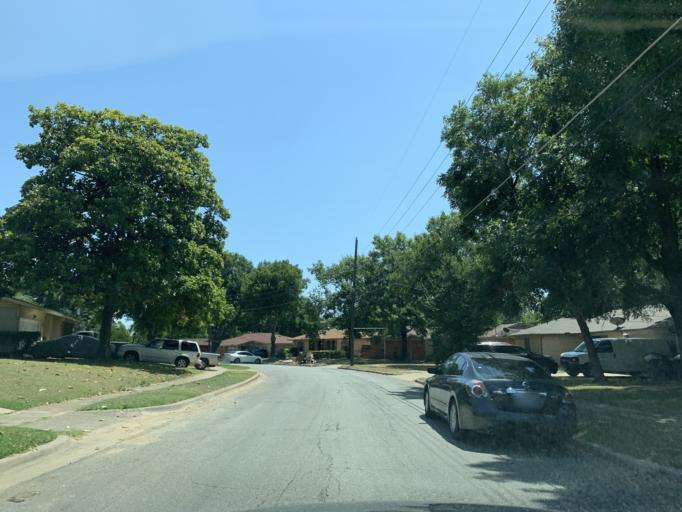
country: US
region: Texas
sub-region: Dallas County
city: Cockrell Hill
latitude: 32.6871
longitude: -96.8080
